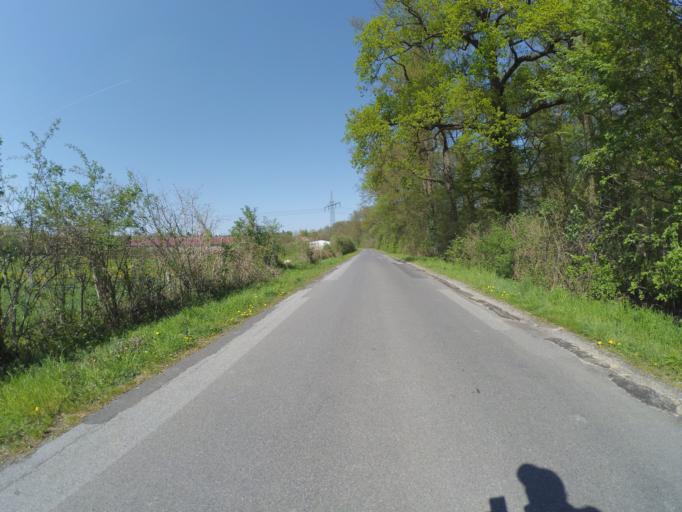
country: DE
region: North Rhine-Westphalia
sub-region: Regierungsbezirk Munster
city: Ascheberg
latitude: 51.8384
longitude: 7.5944
